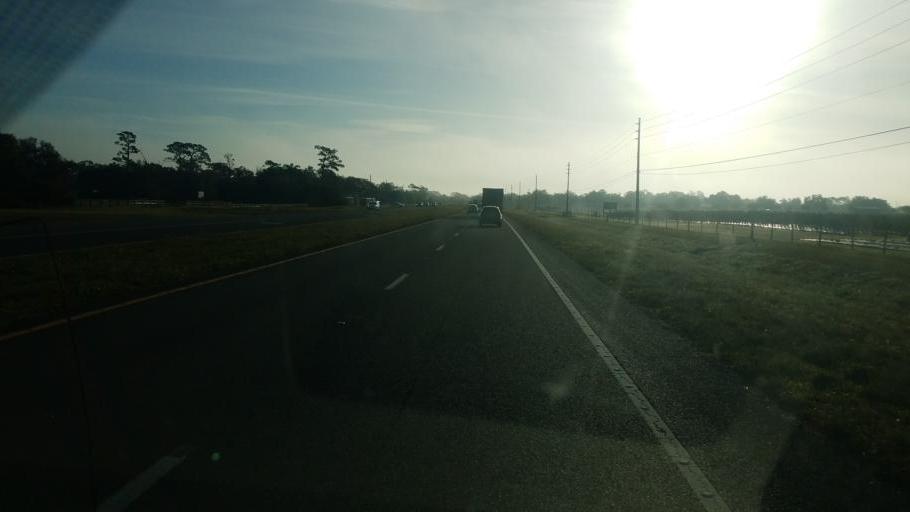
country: US
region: Florida
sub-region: Osceola County
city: Saint Cloud
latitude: 28.2426
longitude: -81.2156
